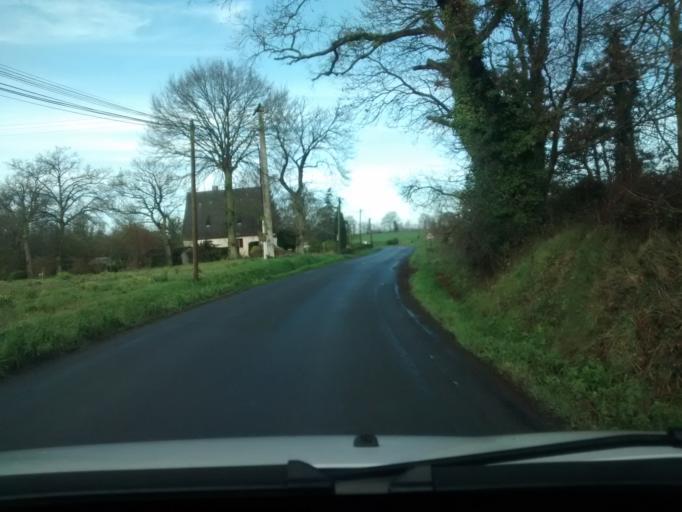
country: FR
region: Brittany
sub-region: Departement d'Ille-et-Vilaine
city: Montgermont
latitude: 48.1440
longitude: -1.7372
